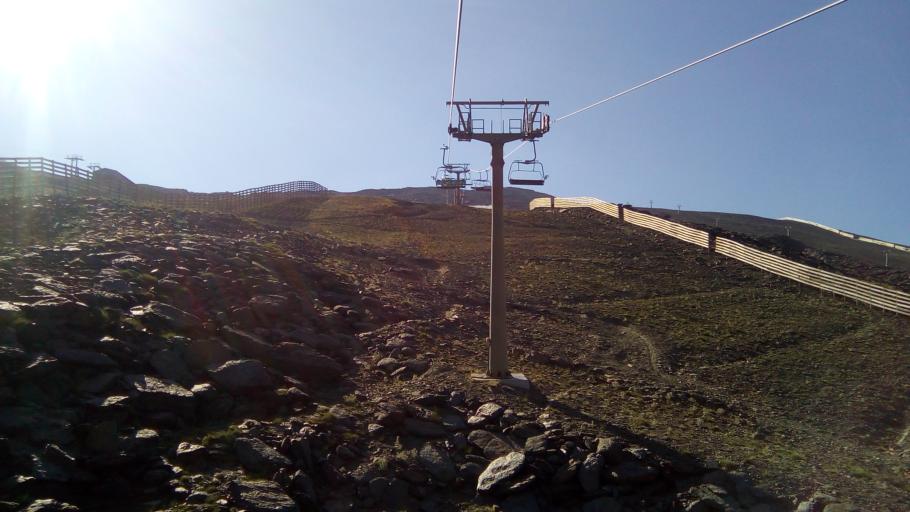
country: ES
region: Andalusia
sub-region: Provincia de Granada
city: Capileira
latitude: 37.0651
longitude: -3.3779
